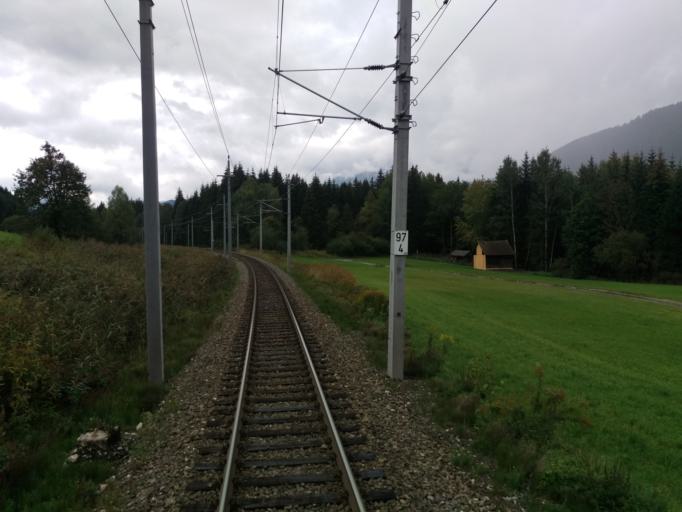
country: AT
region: Styria
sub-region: Politischer Bezirk Liezen
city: Selzthal
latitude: 47.5494
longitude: 14.2960
